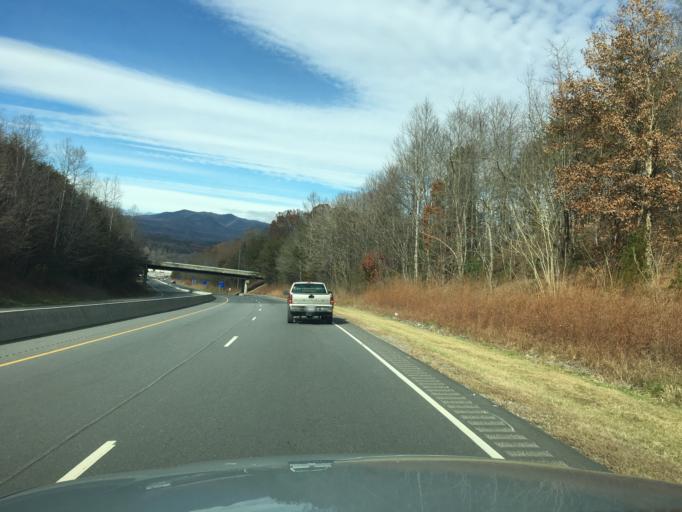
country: US
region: North Carolina
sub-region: McDowell County
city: Marion
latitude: 35.6973
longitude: -82.0303
